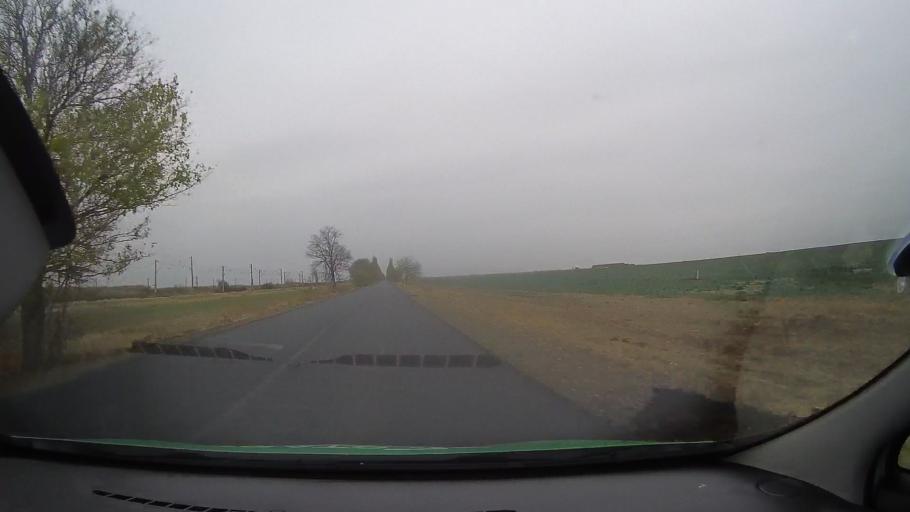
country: RO
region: Ialomita
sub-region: Comuna Valea Ciorii
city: Valea Ciorii
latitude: 44.7056
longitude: 27.5949
